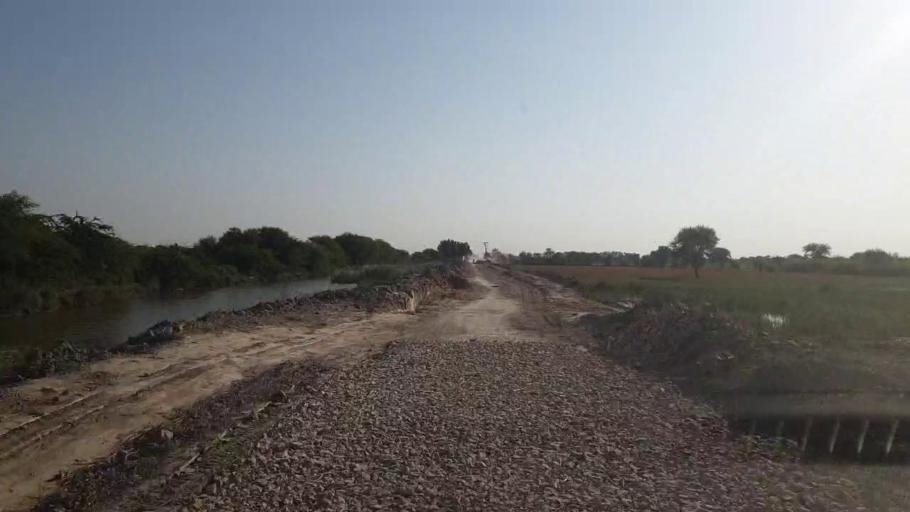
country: PK
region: Sindh
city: Talhar
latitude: 24.9270
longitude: 68.7481
